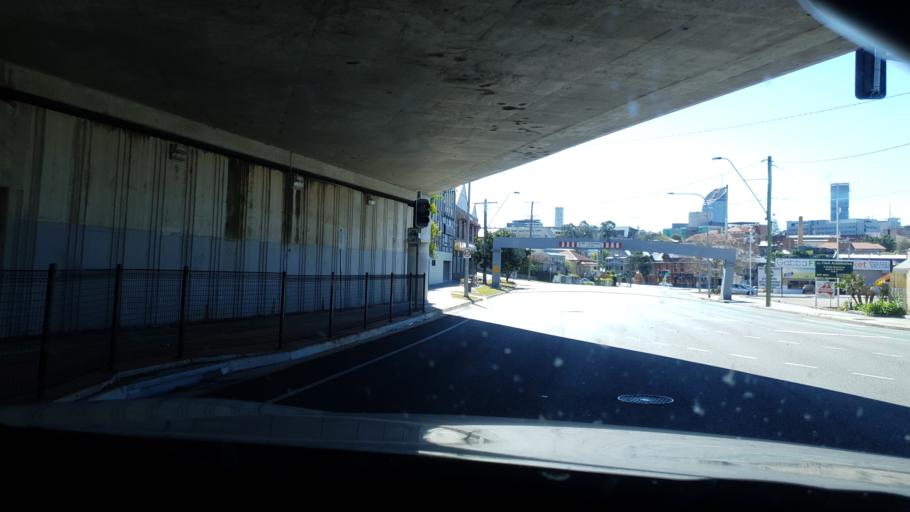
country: AU
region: Queensland
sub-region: Brisbane
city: Woolloongabba
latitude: -27.4918
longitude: 153.0274
